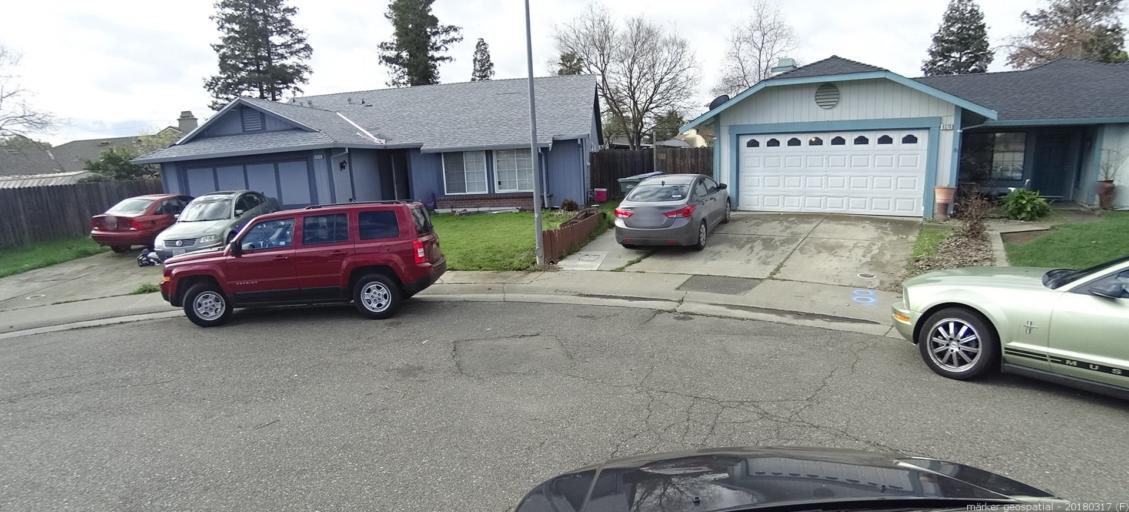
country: US
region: California
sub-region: Sacramento County
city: Florin
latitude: 38.4661
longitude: -121.3960
